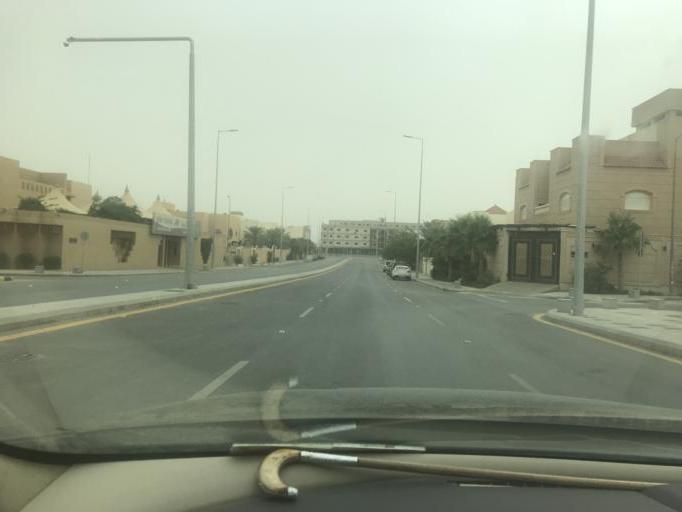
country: SA
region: Ar Riyad
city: Riyadh
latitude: 24.7266
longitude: 46.7881
